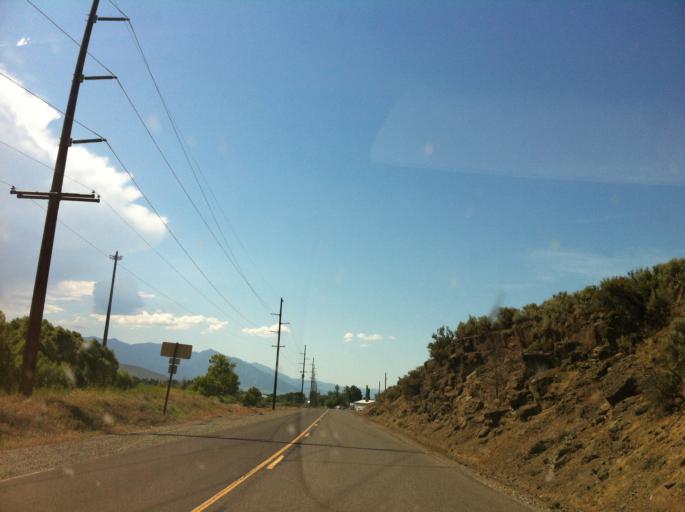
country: US
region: Oregon
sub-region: Baker County
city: Baker City
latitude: 44.7238
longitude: -117.7797
